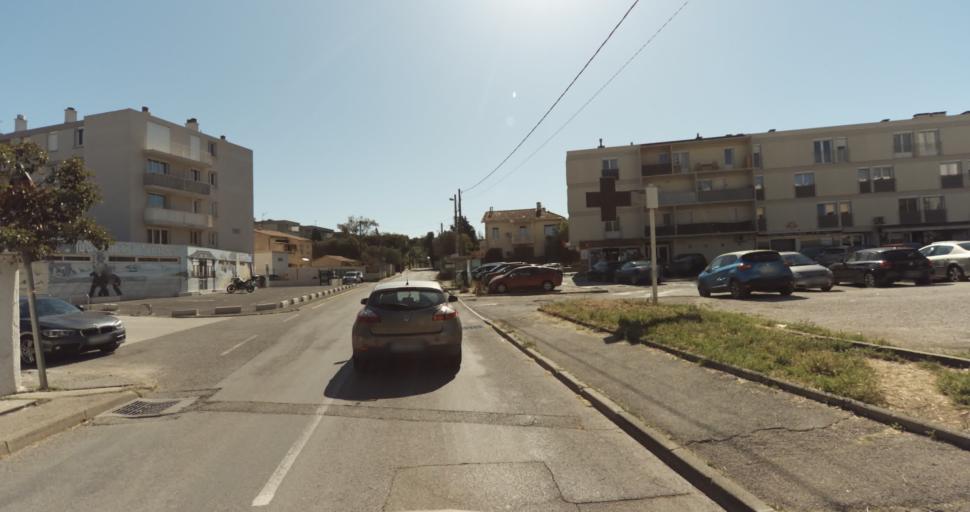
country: FR
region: Provence-Alpes-Cote d'Azur
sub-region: Departement du Var
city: La Seyne-sur-Mer
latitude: 43.0989
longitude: 5.9008
